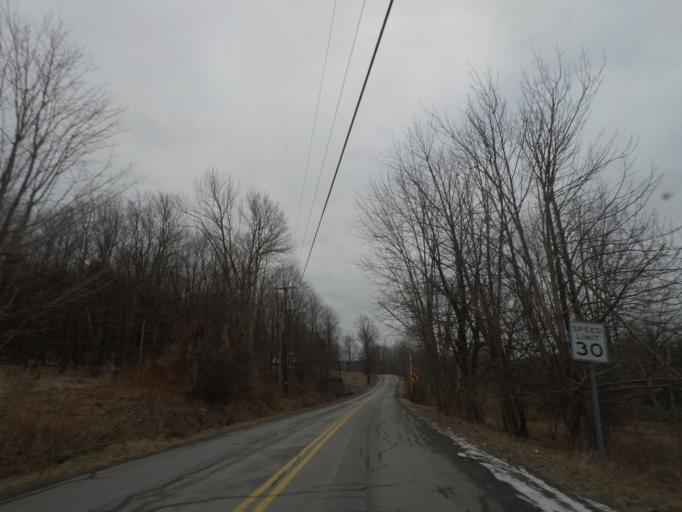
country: US
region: New York
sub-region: Rensselaer County
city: Poestenkill
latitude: 42.7689
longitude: -73.4511
